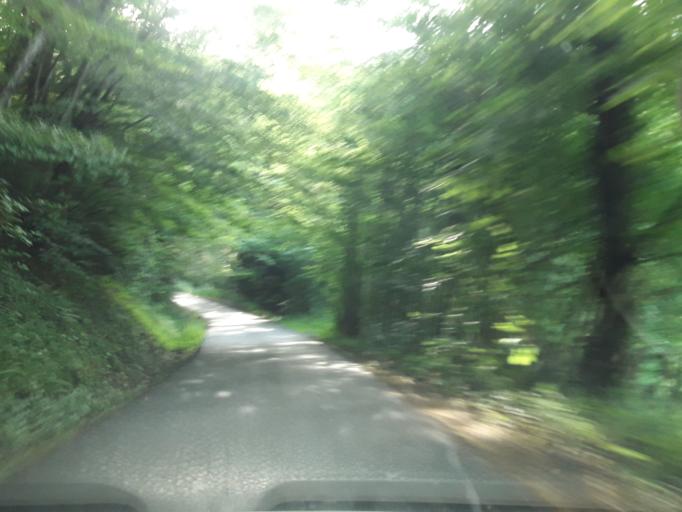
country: FR
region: Rhone-Alpes
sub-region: Departement du Rhone
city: Bessenay
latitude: 45.7581
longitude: 4.5224
